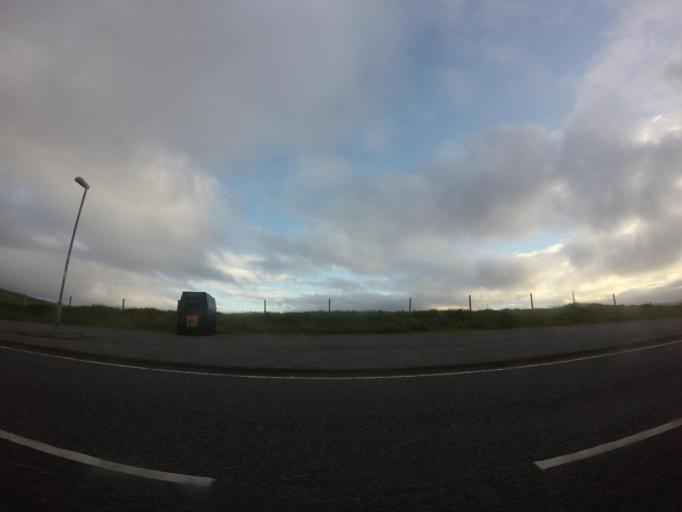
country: GB
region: Scotland
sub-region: Eilean Siar
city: Stornoway
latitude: 58.2047
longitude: -6.2846
